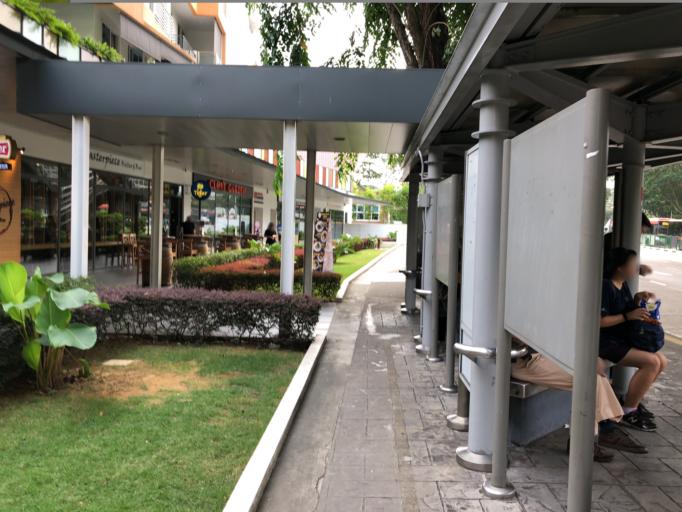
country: SG
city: Singapore
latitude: 1.3212
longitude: 103.8418
